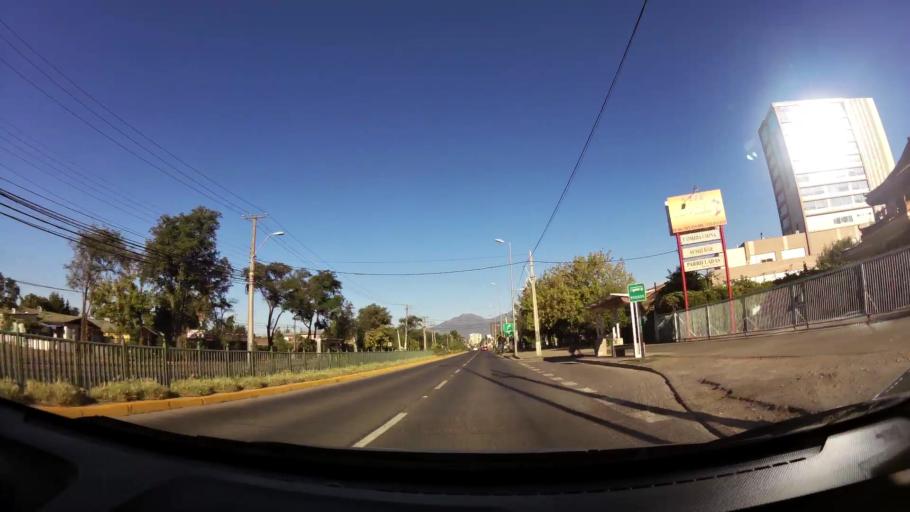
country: CL
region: O'Higgins
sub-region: Provincia de Cachapoal
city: Rancagua
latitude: -34.1740
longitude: -70.7157
